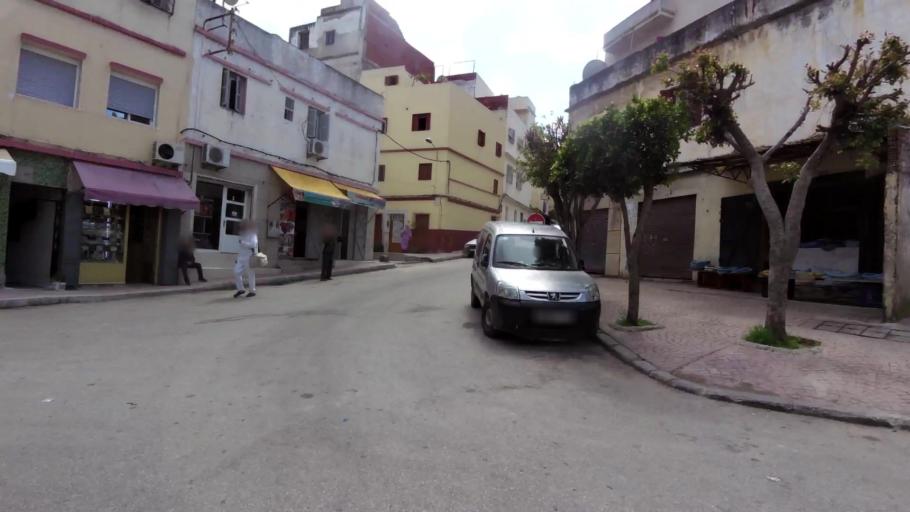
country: MA
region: Tanger-Tetouan
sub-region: Tanger-Assilah
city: Tangier
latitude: 35.7602
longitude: -5.8137
